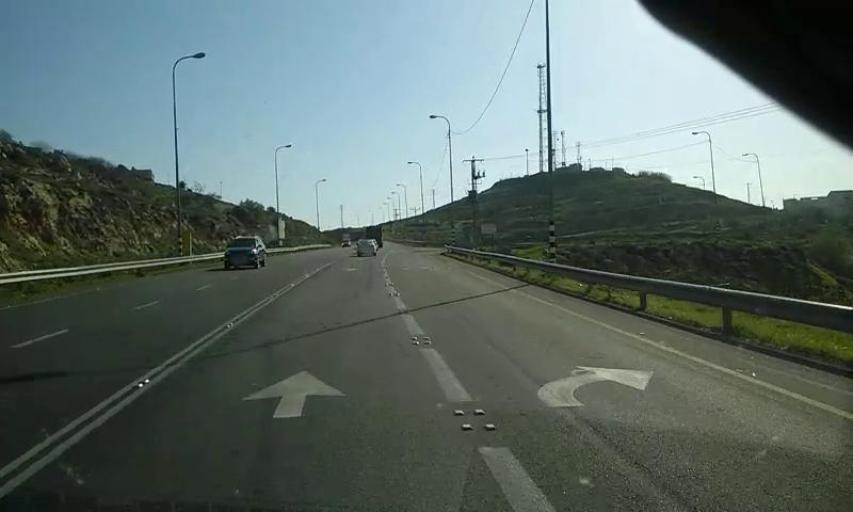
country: PS
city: Al Buq`ah
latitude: 31.5295
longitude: 35.1299
